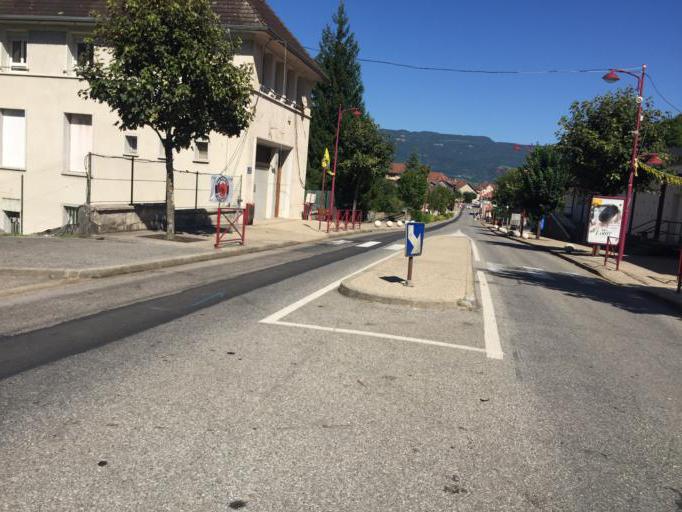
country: FR
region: Rhone-Alpes
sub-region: Departement de l'Ain
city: Culoz
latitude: 45.8487
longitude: 5.7768
